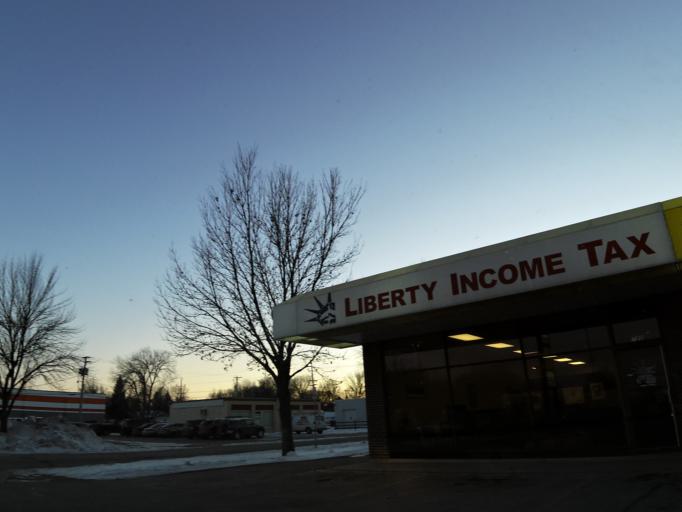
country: US
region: North Dakota
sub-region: Grand Forks County
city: Grand Forks
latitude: 47.9145
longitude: -97.0453
